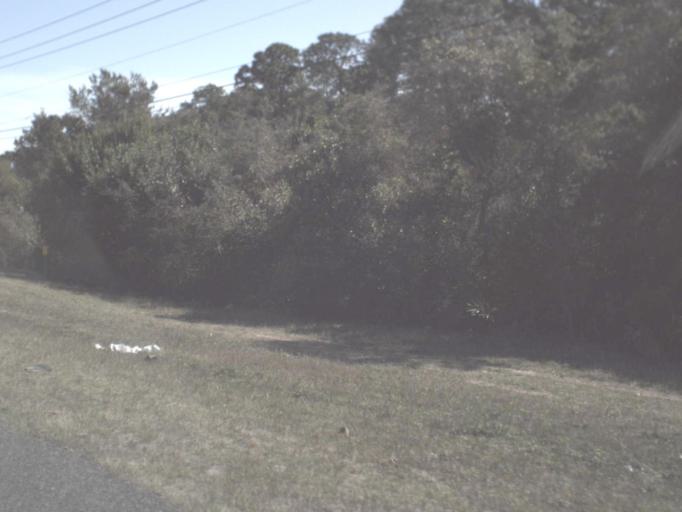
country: US
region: Florida
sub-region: Bay County
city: Laguna Beach
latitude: 30.2416
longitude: -85.9154
